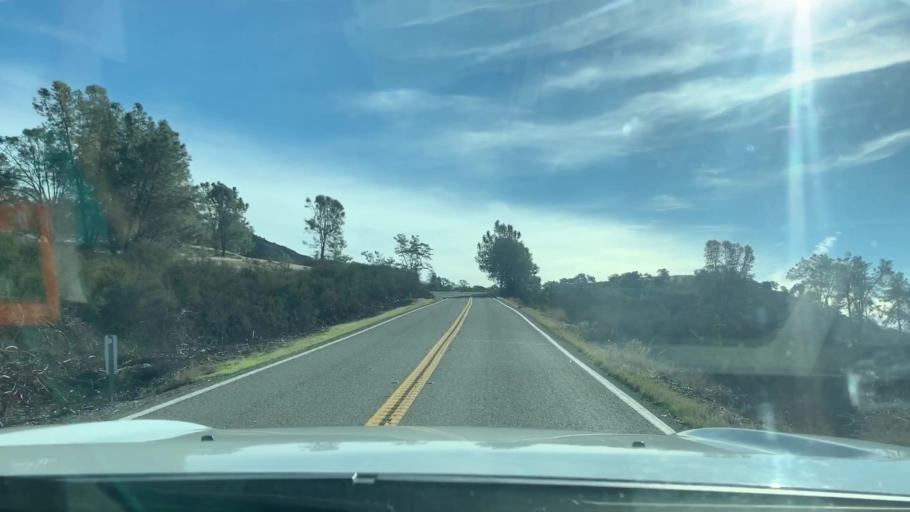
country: US
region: California
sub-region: Monterey County
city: King City
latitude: 36.1997
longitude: -120.7923
